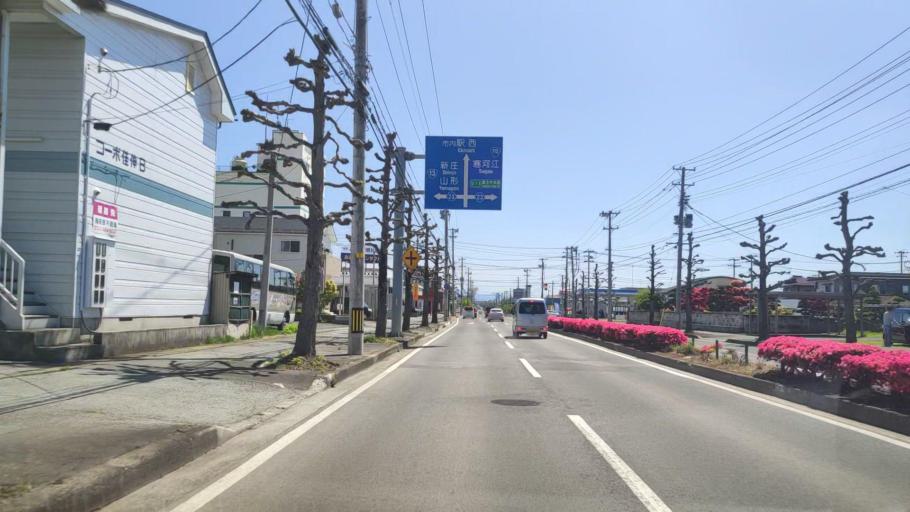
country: JP
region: Yamagata
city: Tendo
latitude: 38.3673
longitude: 140.3675
